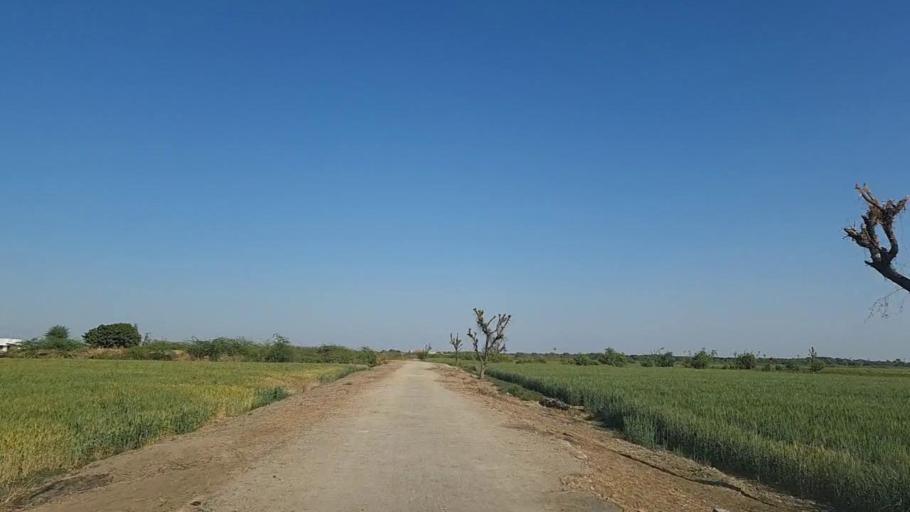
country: PK
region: Sindh
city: Kunri
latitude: 25.2490
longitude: 69.4962
